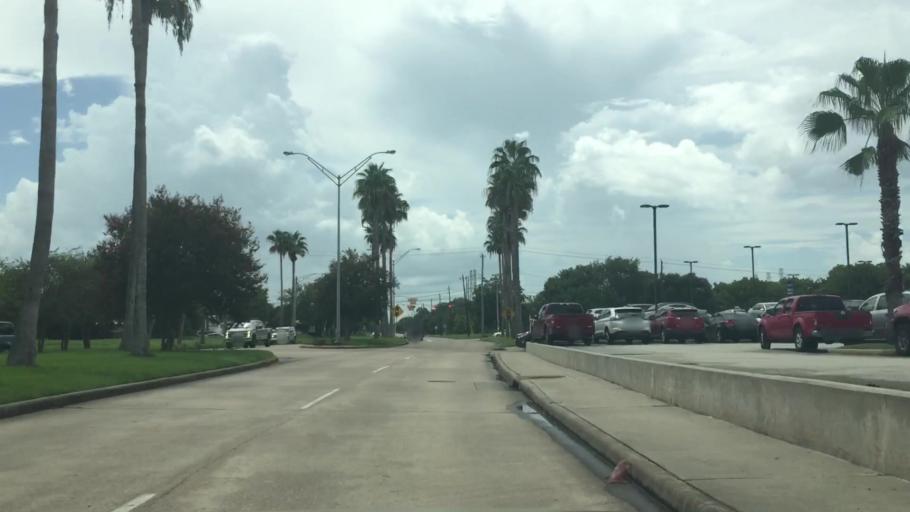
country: US
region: Texas
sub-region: Harris County
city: Webster
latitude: 29.5397
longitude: -95.1282
